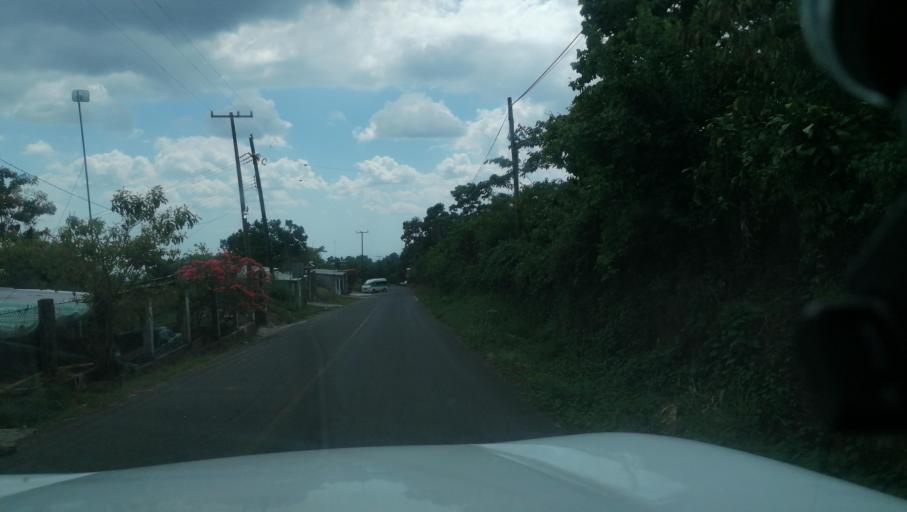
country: MX
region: Chiapas
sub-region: Cacahoatan
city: Benito Juarez
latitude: 15.0395
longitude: -92.1529
